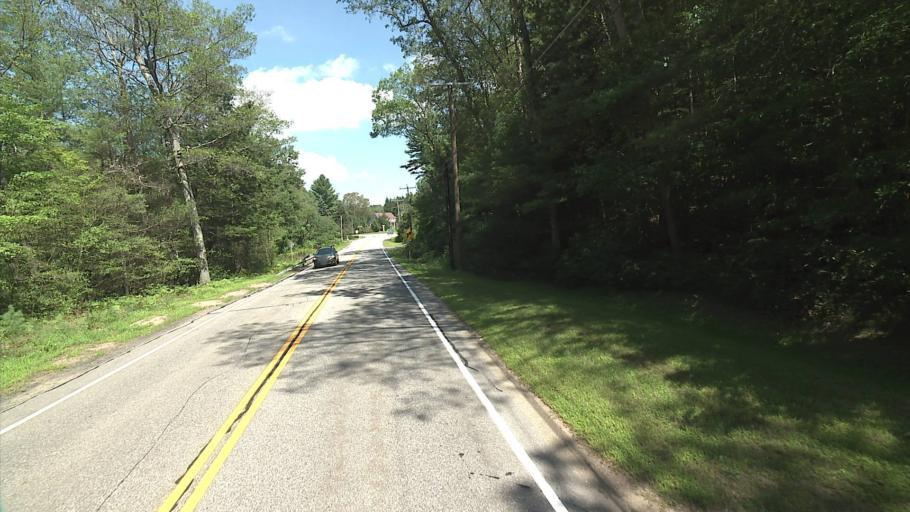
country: US
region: Connecticut
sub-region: Windham County
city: South Woodstock
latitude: 41.9276
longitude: -72.0830
